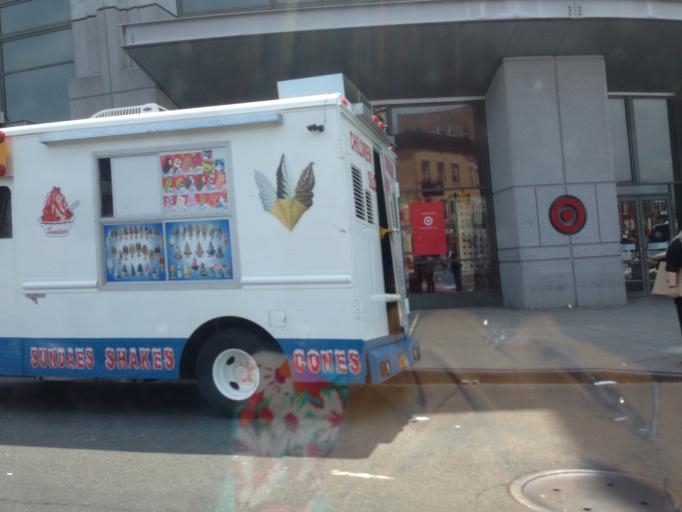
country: US
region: New York
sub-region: Kings County
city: Brooklyn
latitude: 40.6316
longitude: -73.9465
